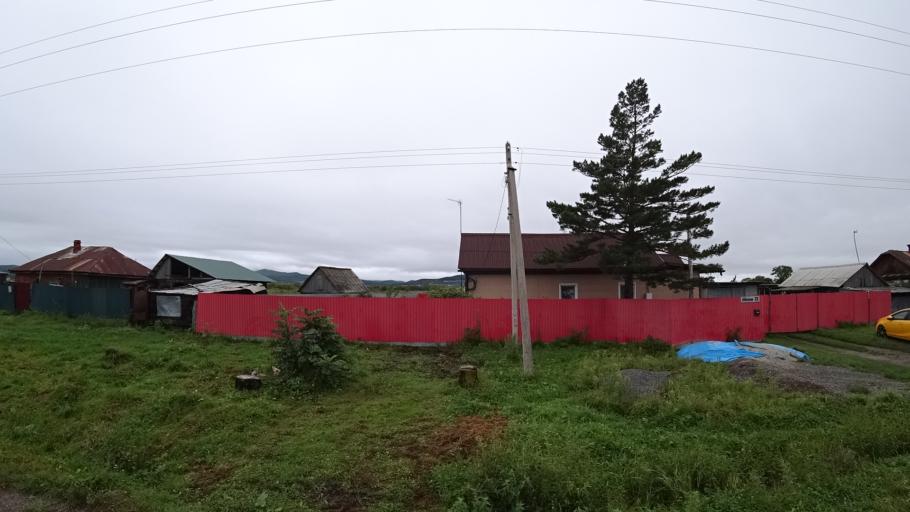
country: RU
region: Primorskiy
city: Monastyrishche
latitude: 44.1970
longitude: 132.4594
